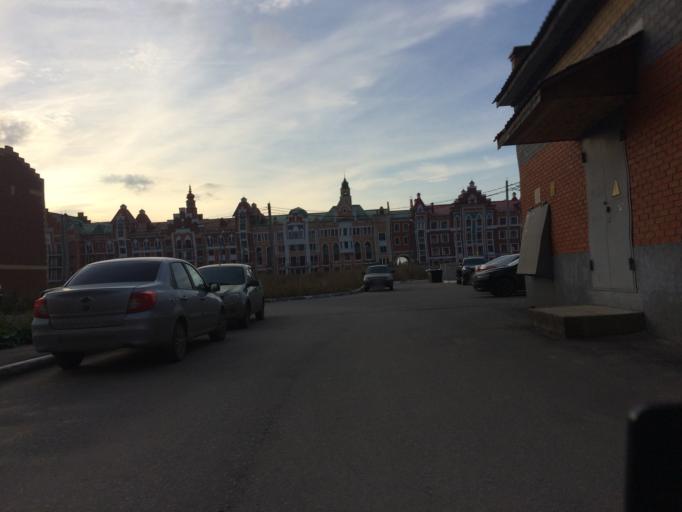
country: RU
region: Mariy-El
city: Yoshkar-Ola
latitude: 56.6345
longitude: 47.9132
